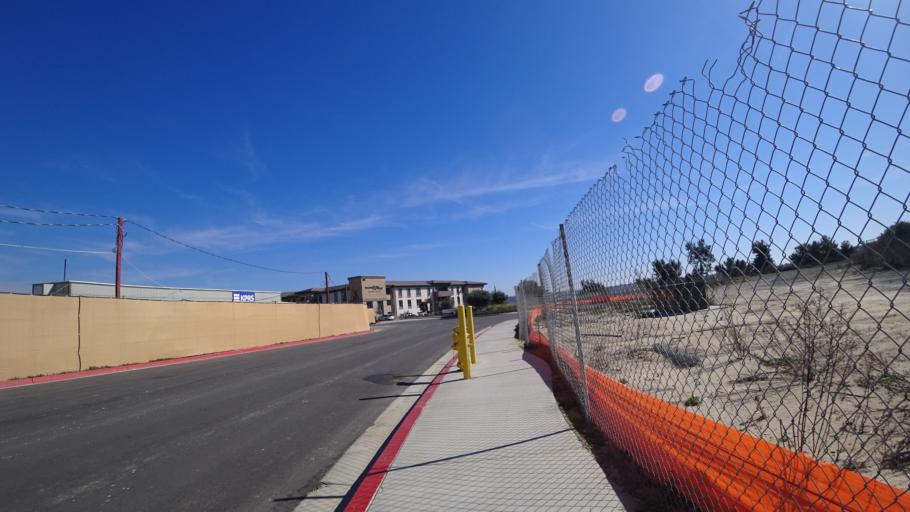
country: US
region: California
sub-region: Orange County
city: Aliso Viejo
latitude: 33.5623
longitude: -117.7283
